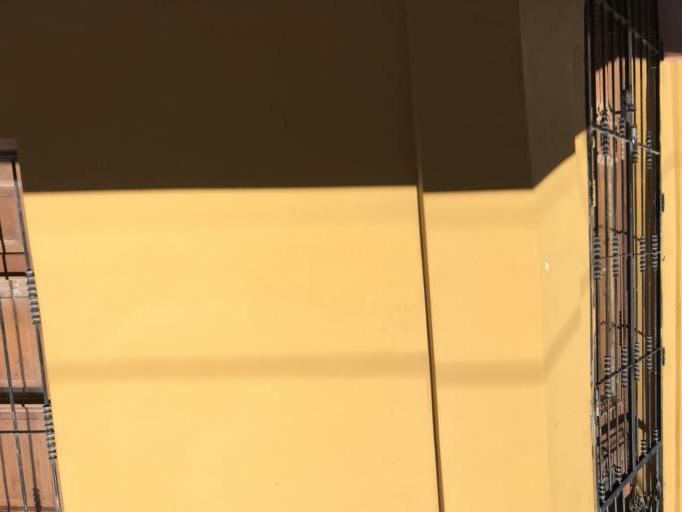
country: AR
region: Jujuy
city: Maimara
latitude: -23.6268
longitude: -65.4088
